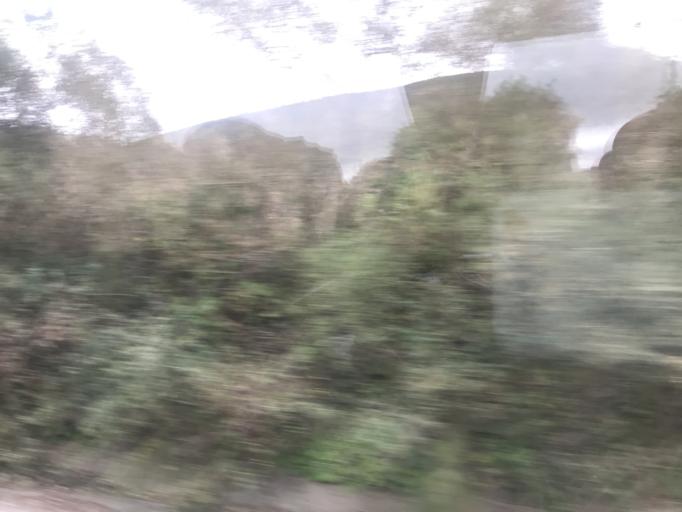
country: TR
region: Balikesir
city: Ergama
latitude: 39.6179
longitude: 27.5618
